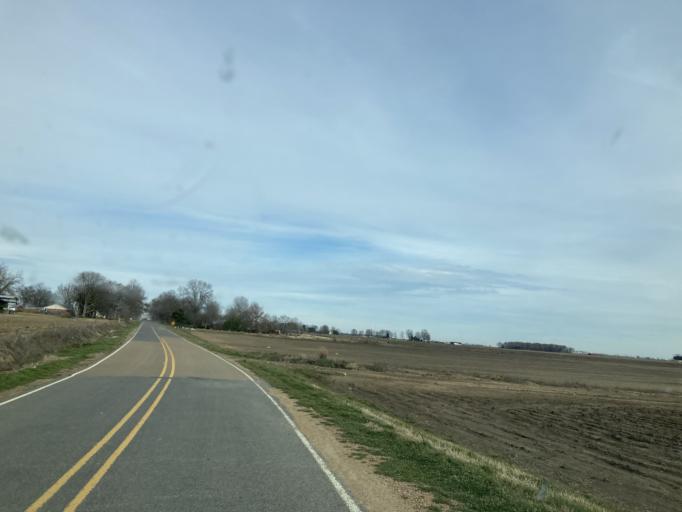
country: US
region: Mississippi
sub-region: Humphreys County
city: Belzoni
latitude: 33.1281
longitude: -90.6112
